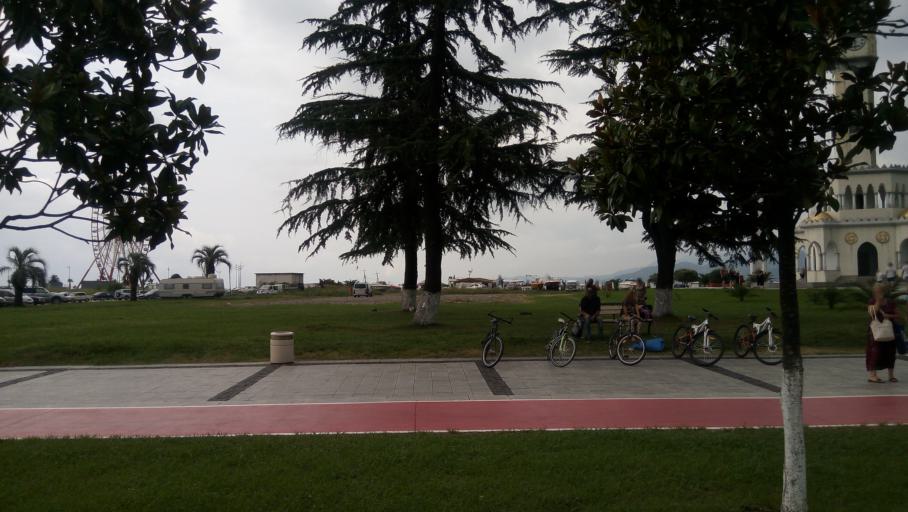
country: GE
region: Ajaria
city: Batumi
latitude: 41.6524
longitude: 41.6420
